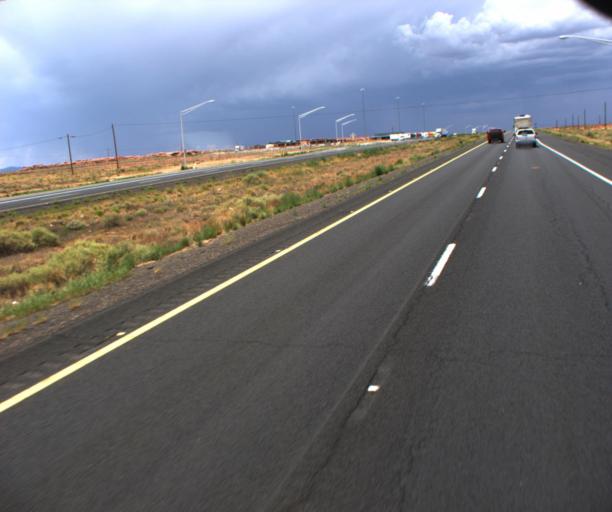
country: US
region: Arizona
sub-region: Coconino County
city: LeChee
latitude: 35.1045
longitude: -110.9992
